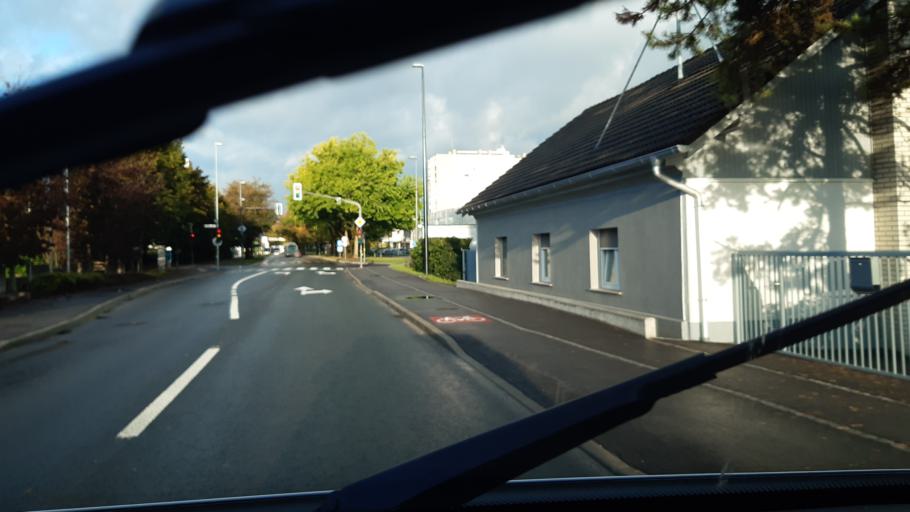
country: SI
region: Ljubljana
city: Ljubljana
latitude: 46.0474
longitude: 14.5490
